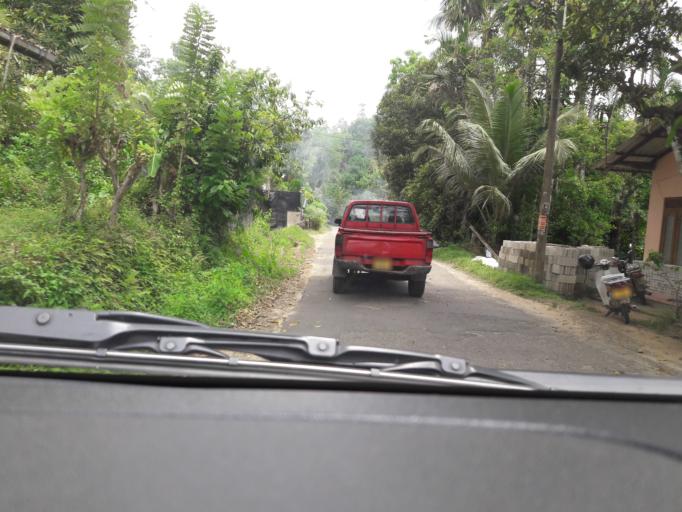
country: LK
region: Southern
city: Galle
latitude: 6.1815
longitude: 80.3034
